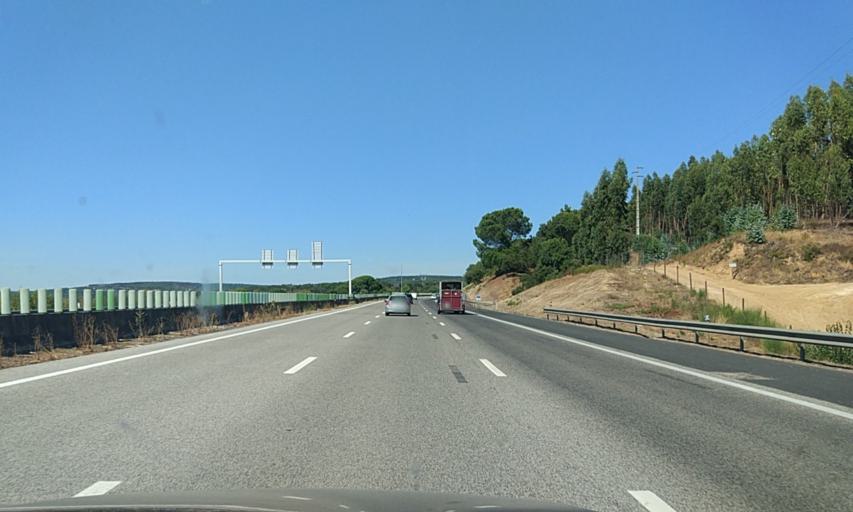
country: PT
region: Lisbon
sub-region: Alenquer
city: Carregado
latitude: 39.0625
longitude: -8.9387
